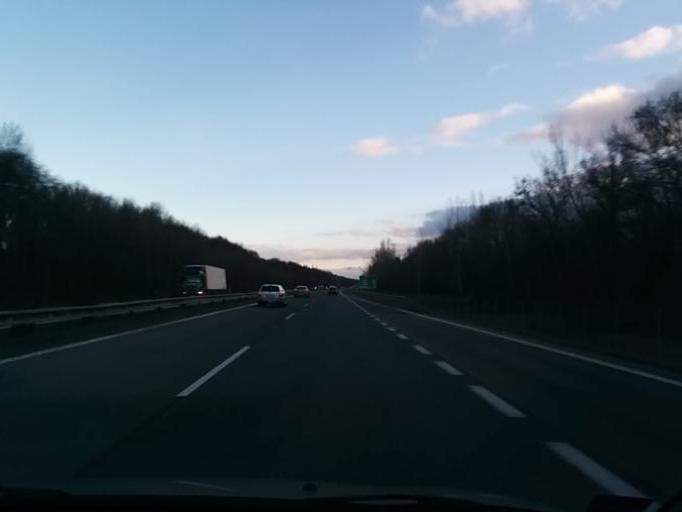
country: SK
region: Trnavsky
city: Leopoldov
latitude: 48.4682
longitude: 17.7420
